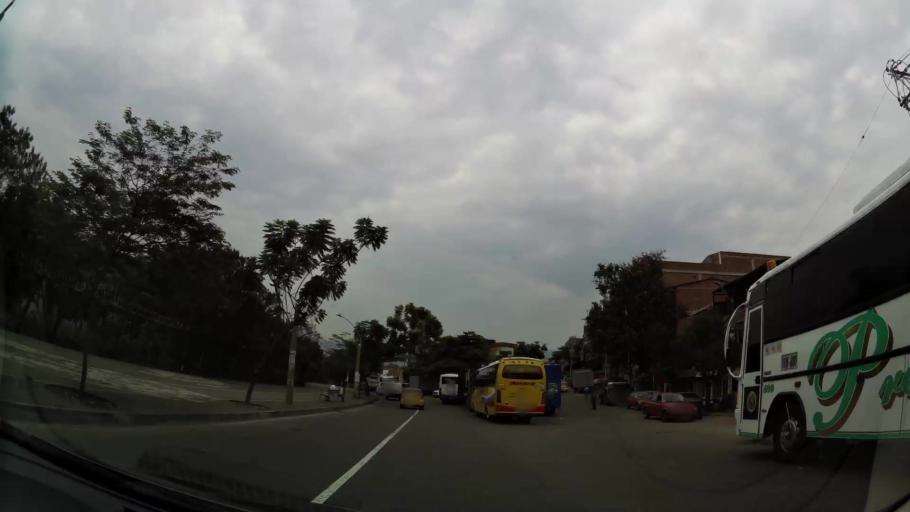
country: CO
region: Antioquia
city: Medellin
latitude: 6.2706
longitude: -75.5619
